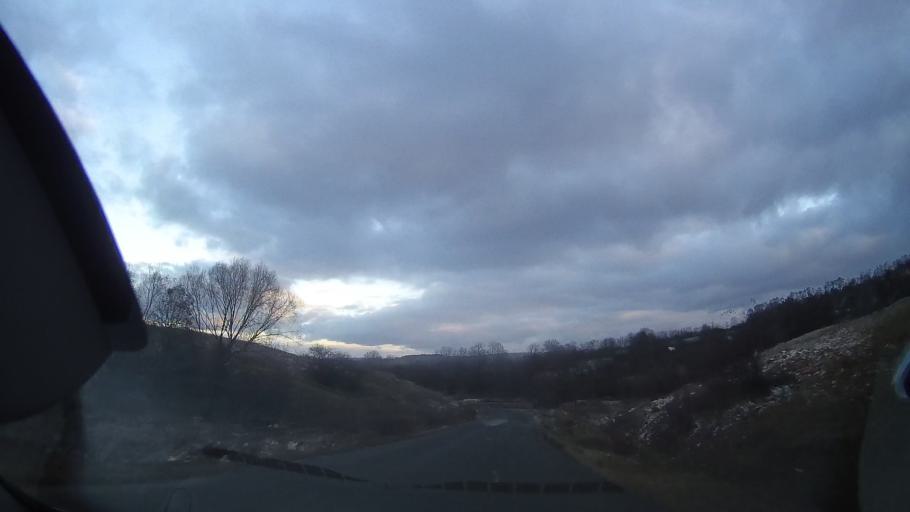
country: RO
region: Cluj
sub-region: Comuna Manastireni
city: Manastireni
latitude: 46.7810
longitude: 23.0686
